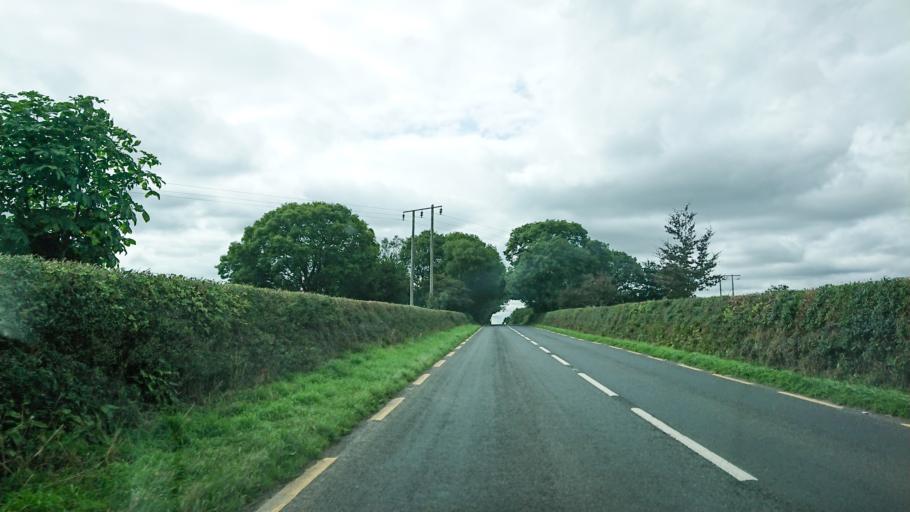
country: IE
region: Munster
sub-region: Waterford
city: Dungarvan
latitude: 52.1100
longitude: -7.6232
